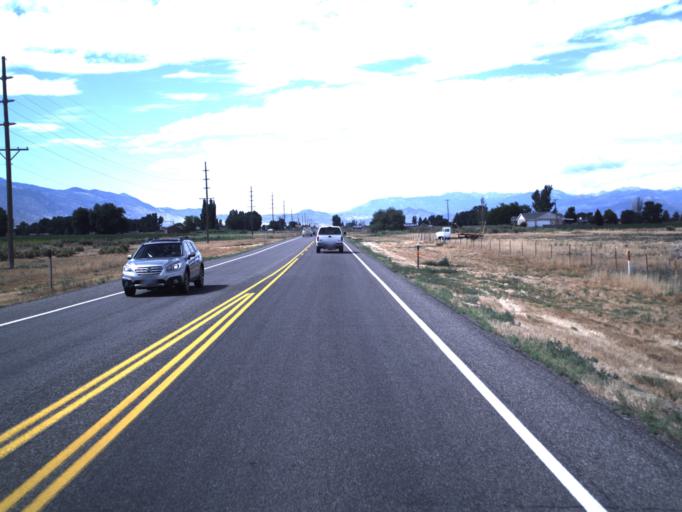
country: US
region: Utah
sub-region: Sevier County
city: Richfield
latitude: 38.7294
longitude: -112.0977
